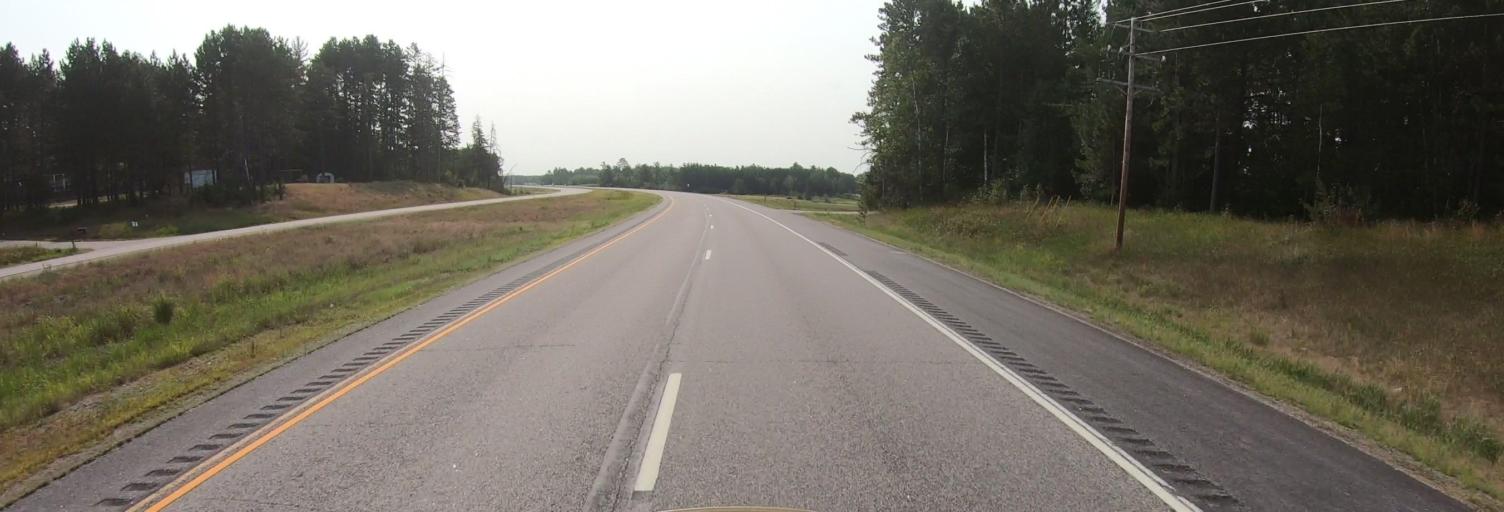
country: US
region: Minnesota
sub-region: Saint Louis County
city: Mountain Iron
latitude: 47.6683
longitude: -92.6440
